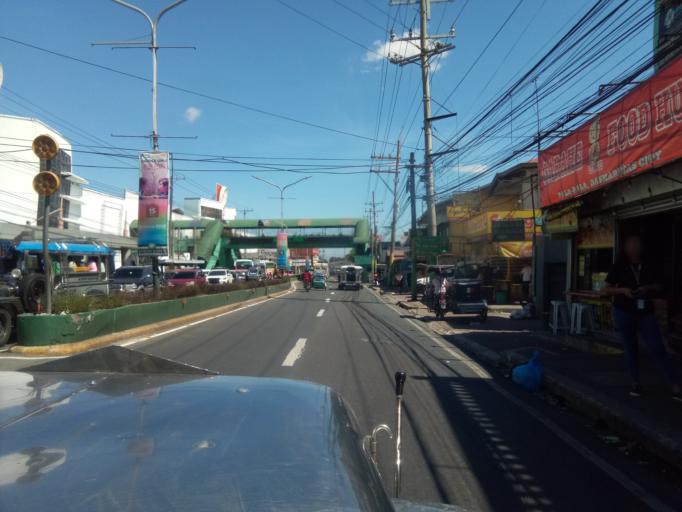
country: PH
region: Calabarzon
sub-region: Province of Cavite
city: Dasmarinas
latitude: 14.2992
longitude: 120.9549
